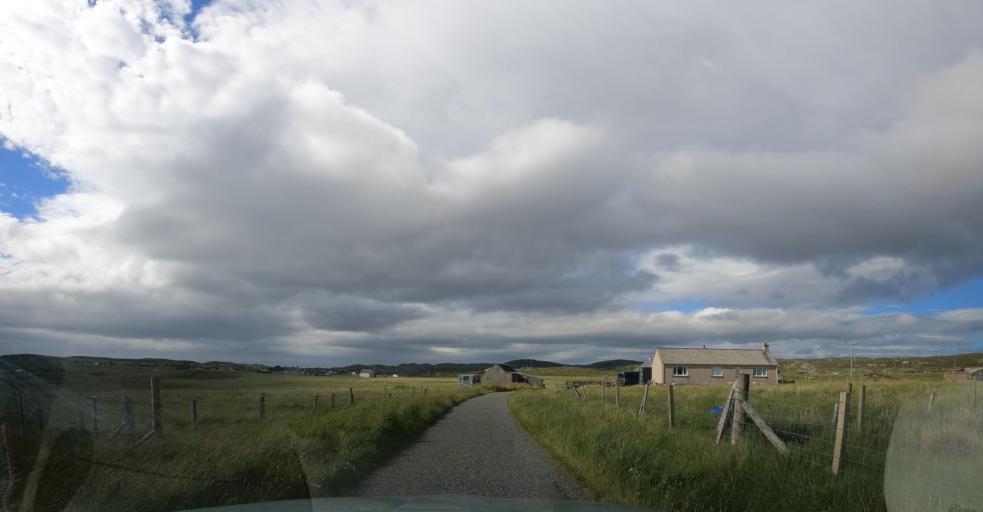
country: GB
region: Scotland
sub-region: Eilean Siar
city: Harris
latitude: 58.1957
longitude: -6.7290
